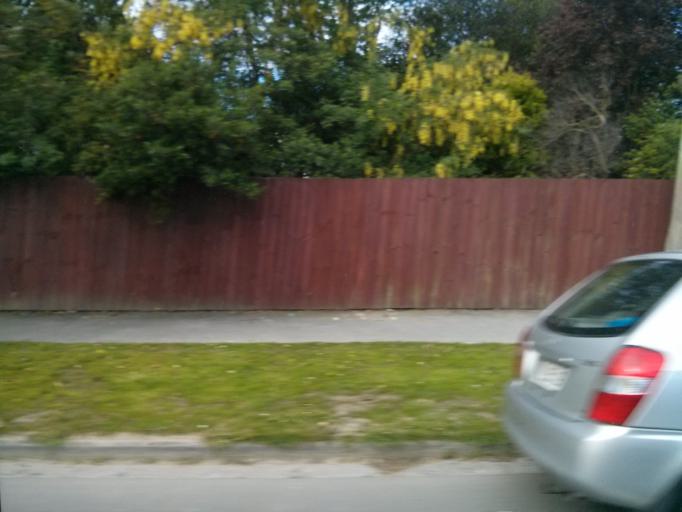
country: NZ
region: Canterbury
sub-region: Christchurch City
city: Christchurch
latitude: -43.5161
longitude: 172.5865
